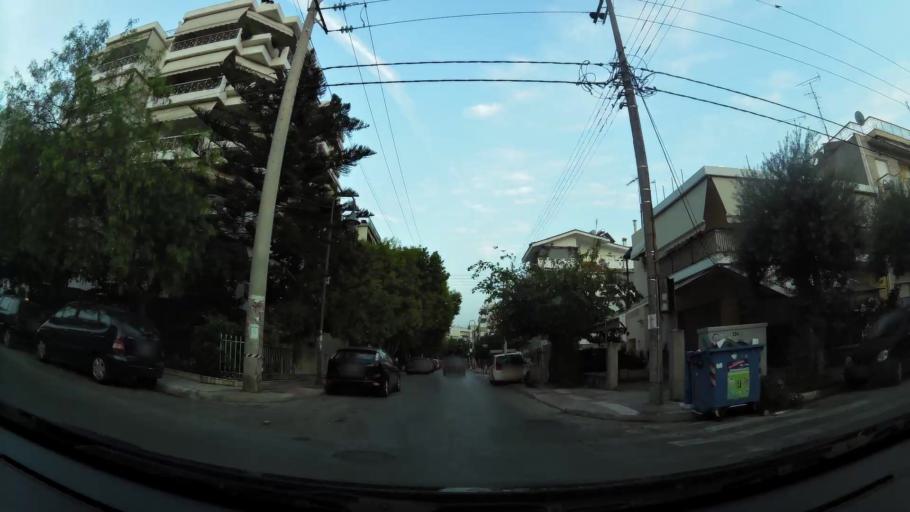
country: GR
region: Attica
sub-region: Nomarchia Athinas
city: Moskhaton
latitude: 37.9526
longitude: 23.6855
